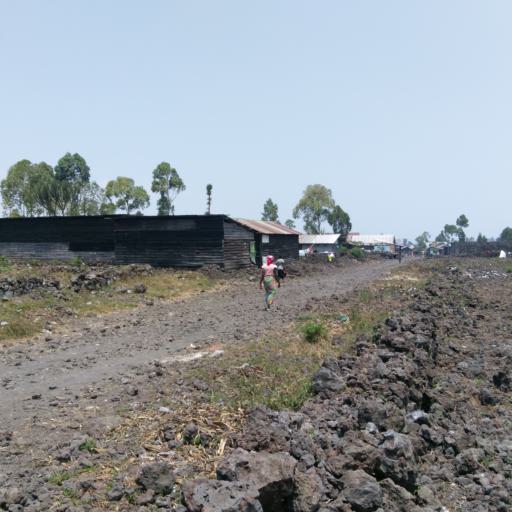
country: CD
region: Nord Kivu
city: Goma
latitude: -1.6457
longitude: 29.2284
